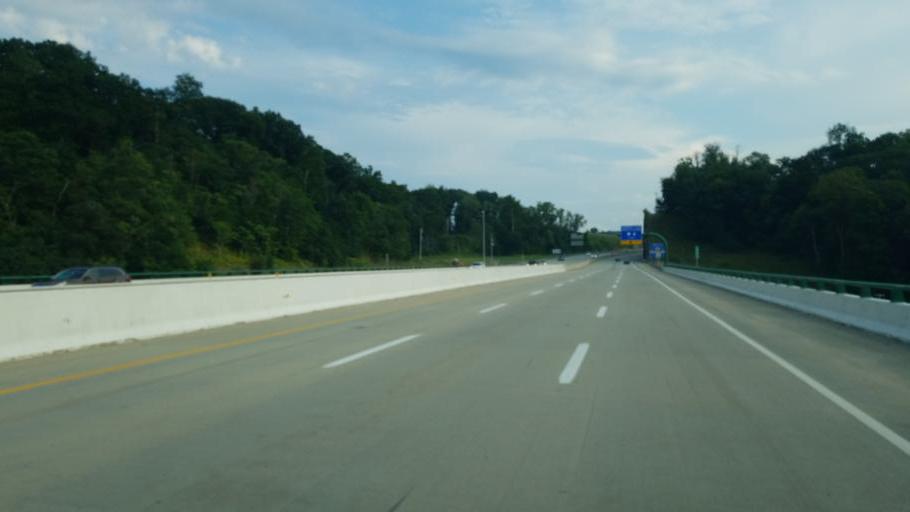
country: US
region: Pennsylvania
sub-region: Allegheny County
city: Cheswick
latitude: 40.5357
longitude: -79.8224
